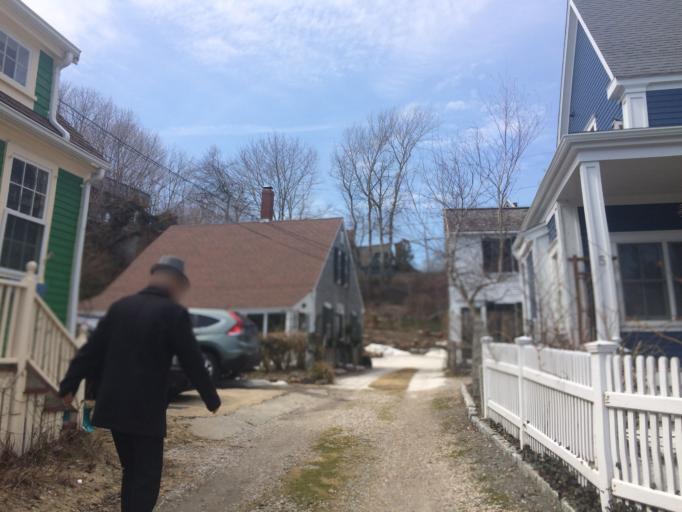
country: US
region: Massachusetts
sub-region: Barnstable County
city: Provincetown
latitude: 42.0557
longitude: -70.1811
